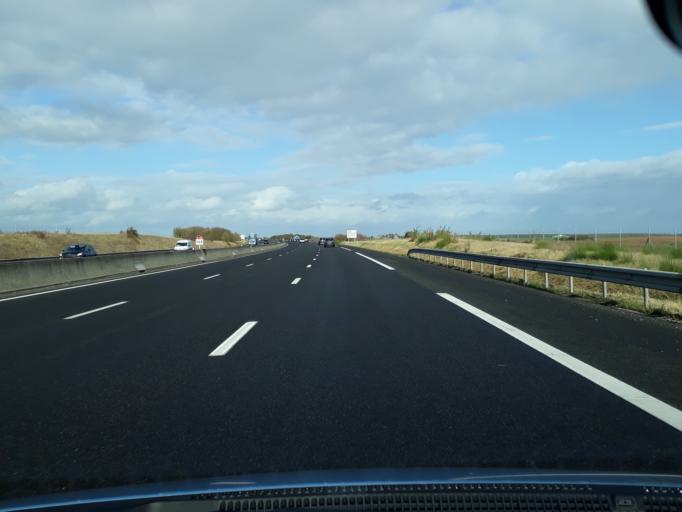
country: FR
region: Centre
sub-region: Departement du Loir-et-Cher
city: La Chaussee-Saint-Victor
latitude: 47.6294
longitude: 1.3527
